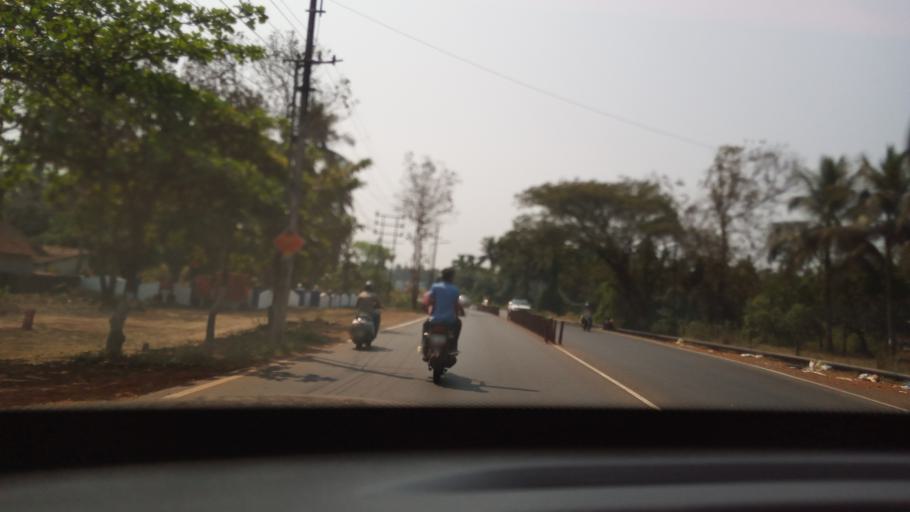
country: IN
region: Goa
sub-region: South Goa
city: Sancoale
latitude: 15.3477
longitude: 73.9271
